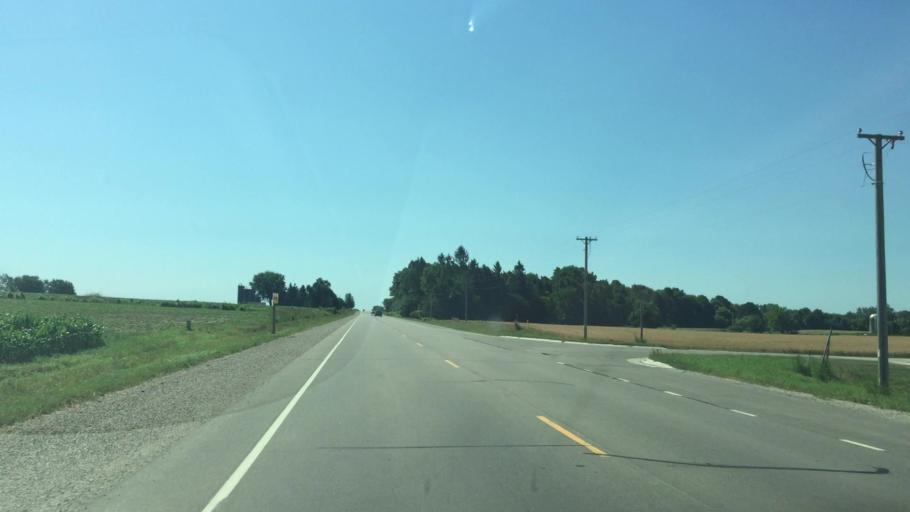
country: US
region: Wisconsin
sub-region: Calumet County
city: Chilton
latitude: 43.9966
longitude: -88.1294
